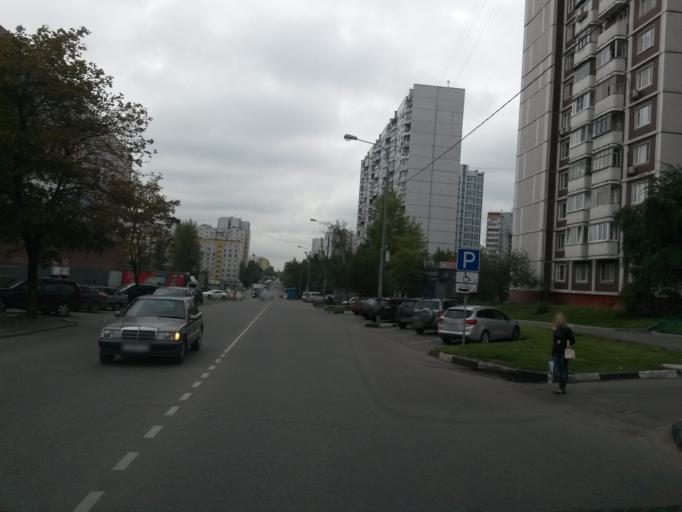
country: RU
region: Moscow
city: Orekhovo-Borisovo
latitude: 55.6124
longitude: 37.7307
